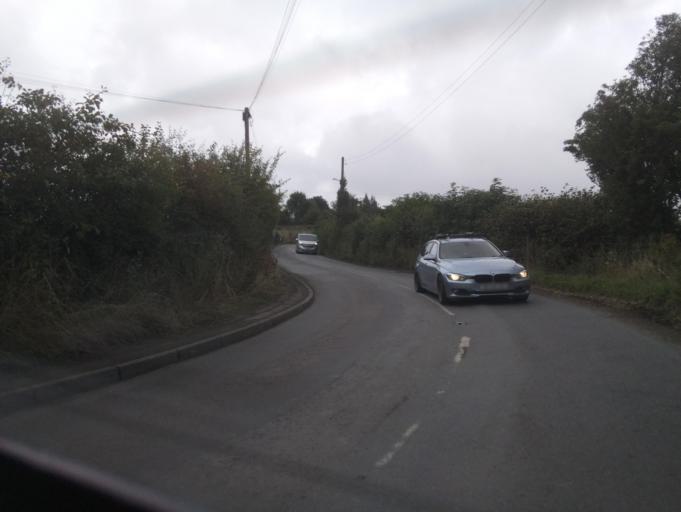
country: GB
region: England
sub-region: Kirklees
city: Shelley
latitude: 53.6067
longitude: -1.6749
